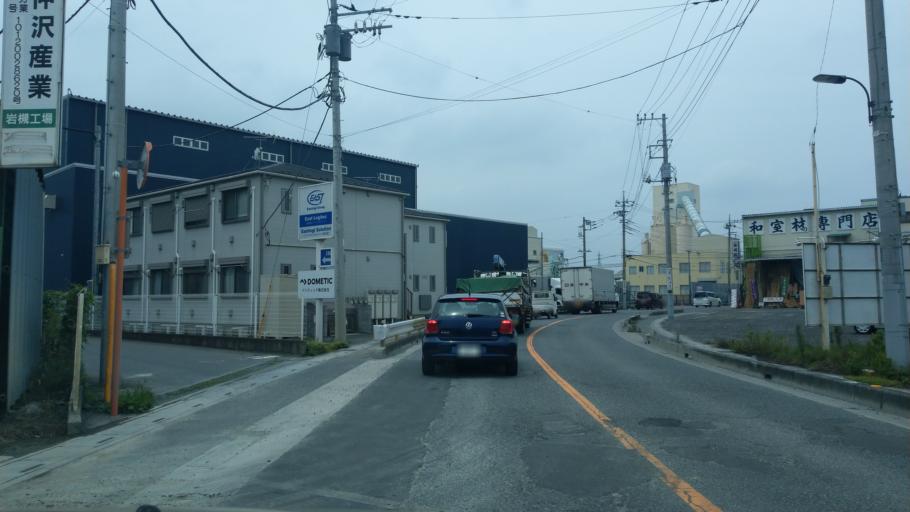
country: JP
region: Saitama
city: Iwatsuki
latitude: 35.9383
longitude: 139.6837
